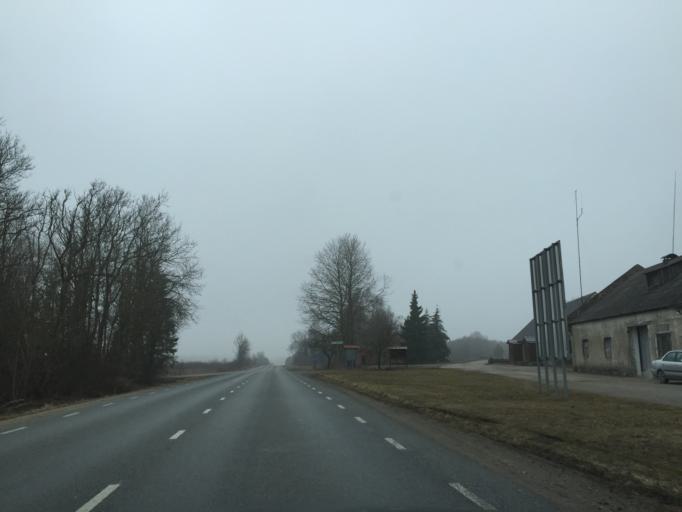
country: EE
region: Laeaene
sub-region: Lihula vald
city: Lihula
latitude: 58.5720
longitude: 23.7434
